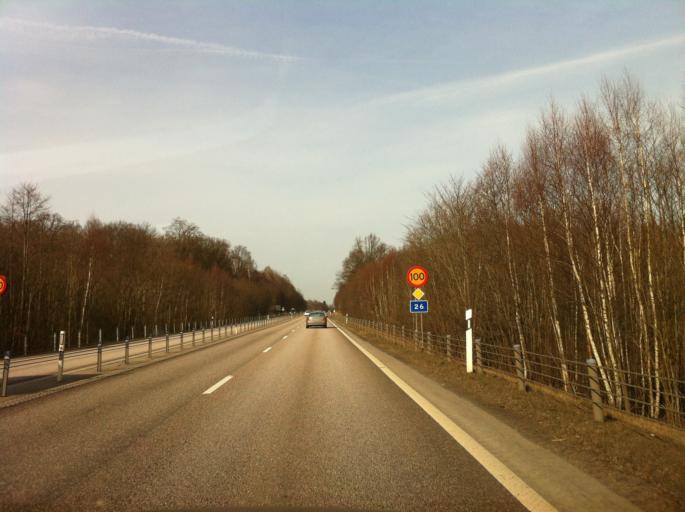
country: SE
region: Vaestra Goetaland
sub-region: Skovde Kommun
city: Stopen
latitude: 58.4535
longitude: 13.8486
